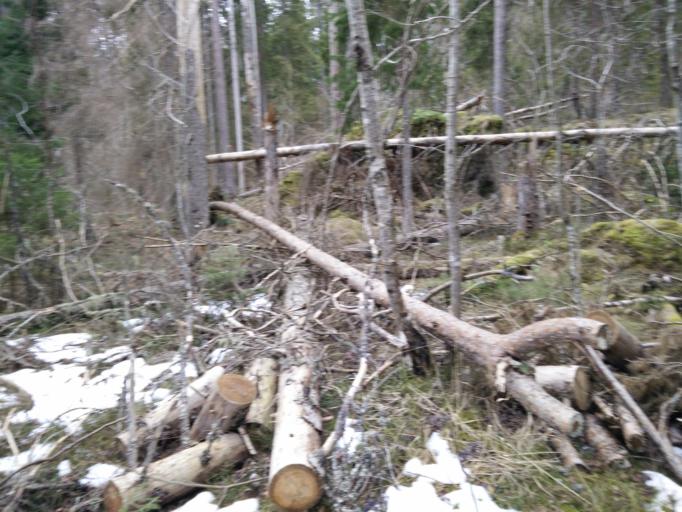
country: SE
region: OErebro
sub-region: Orebro Kommun
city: Garphyttan
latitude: 59.2818
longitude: 14.8944
